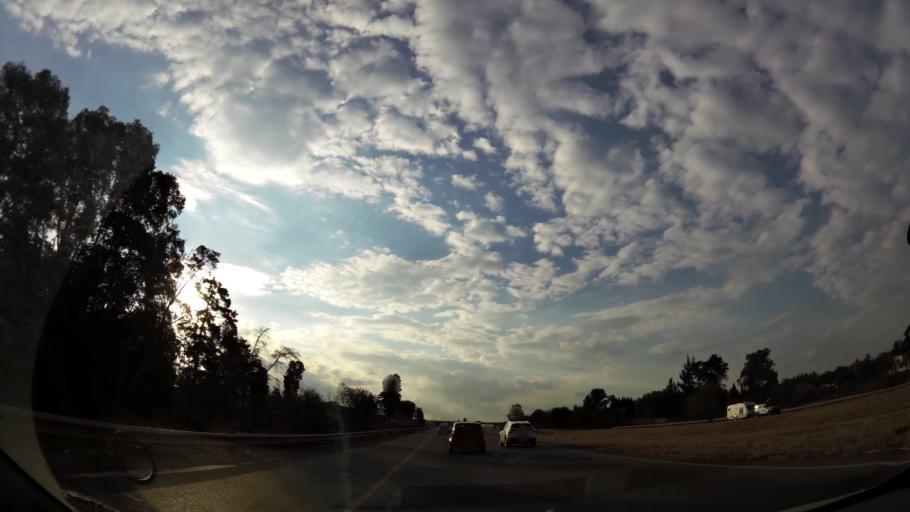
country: ZA
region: Gauteng
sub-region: Sedibeng District Municipality
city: Vanderbijlpark
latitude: -26.7441
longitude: 27.8250
